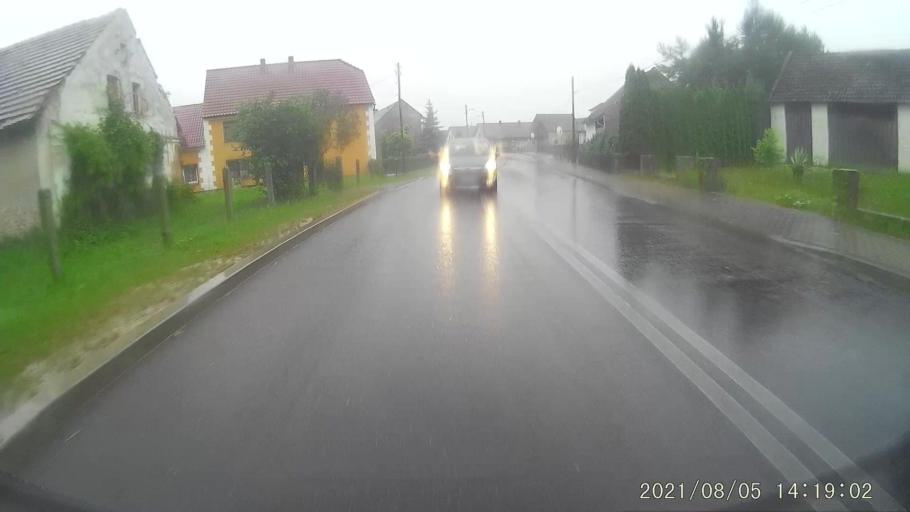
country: PL
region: Opole Voivodeship
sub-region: Powiat prudnicki
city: Biala
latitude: 50.4655
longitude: 17.6894
